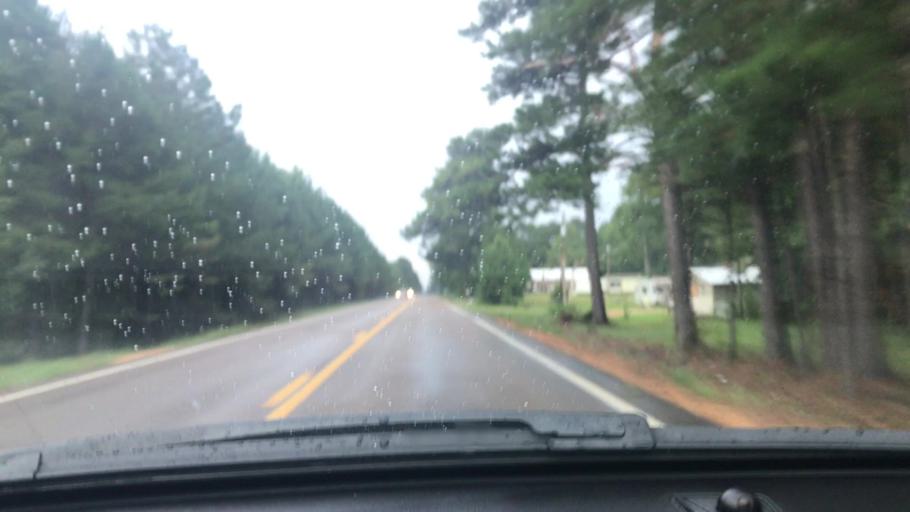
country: US
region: Mississippi
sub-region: Pike County
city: Summit
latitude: 31.3440
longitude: -90.5868
